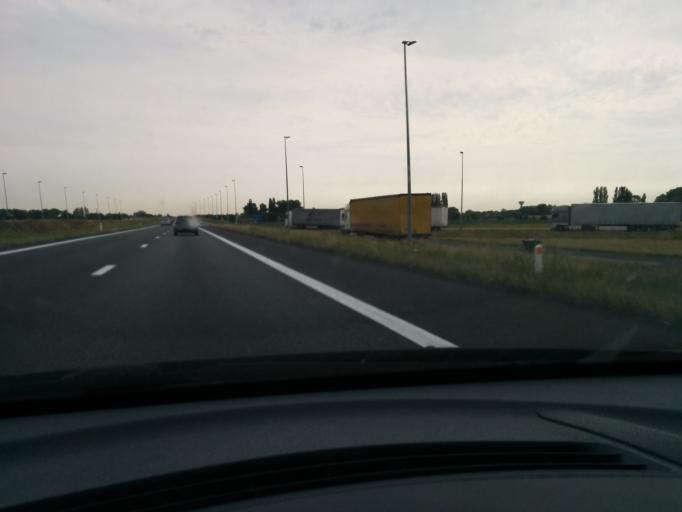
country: BE
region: Flanders
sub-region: Provincie West-Vlaanderen
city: Oudenburg
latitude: 51.1728
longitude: 2.9962
